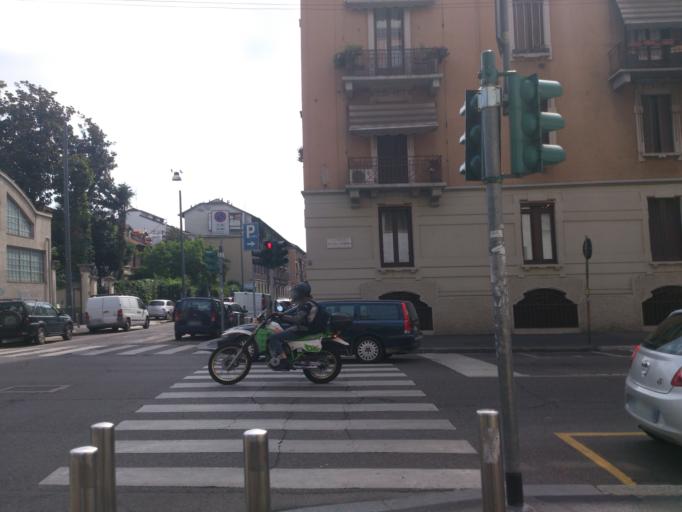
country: IT
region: Lombardy
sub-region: Citta metropolitana di Milano
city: Milano
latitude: 45.4639
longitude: 9.2112
